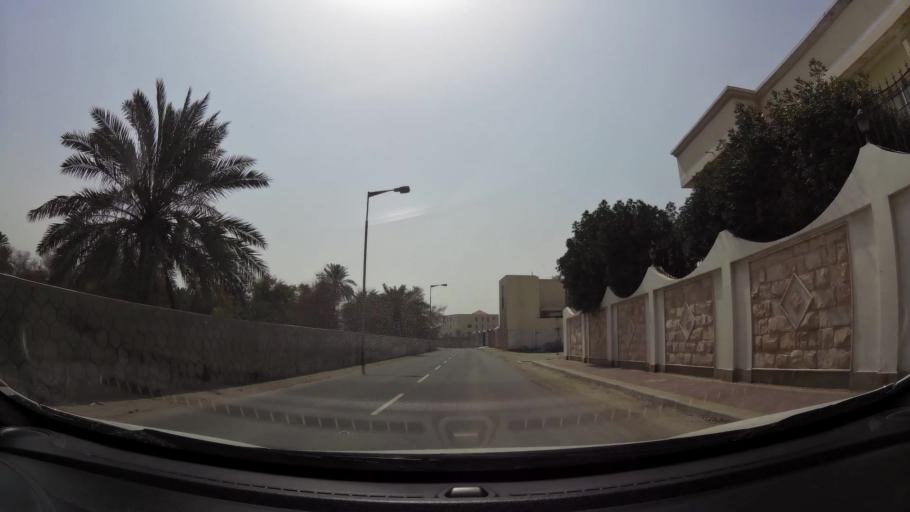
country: BH
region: Manama
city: Jidd Hafs
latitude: 26.2231
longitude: 50.5044
